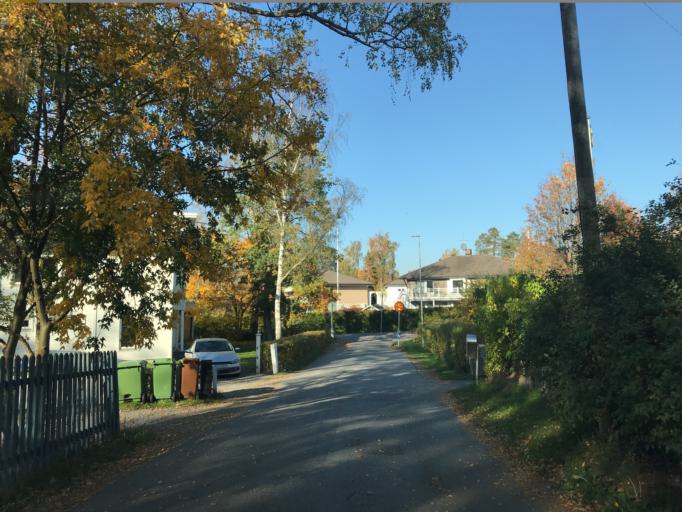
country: SE
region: Stockholm
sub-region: Sollentuna Kommun
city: Sollentuna
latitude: 59.4267
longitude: 17.9309
